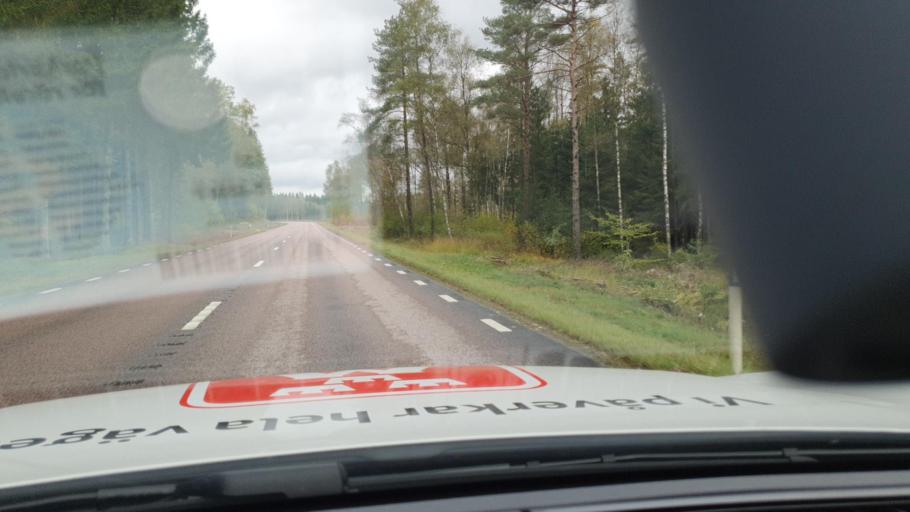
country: SE
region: Halland
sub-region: Halmstads Kommun
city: Getinge
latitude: 57.1218
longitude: 12.7670
